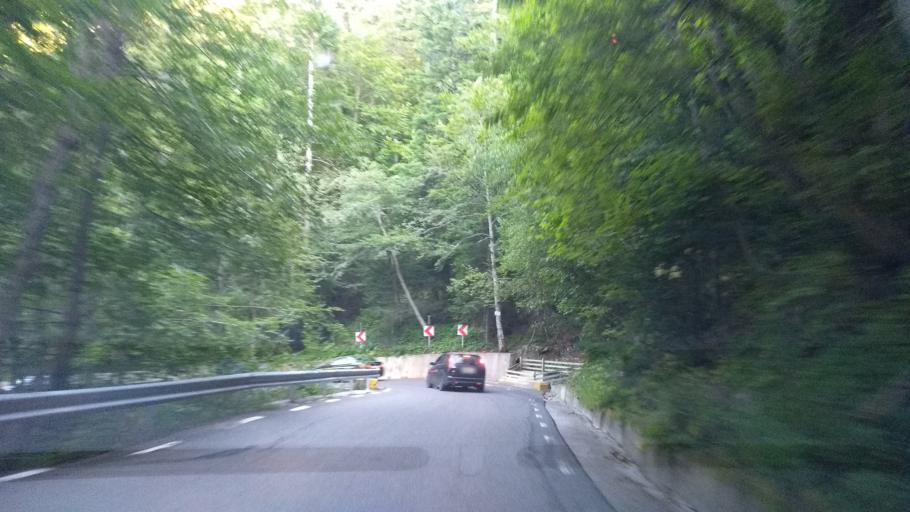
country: RO
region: Prahova
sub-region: Oras Sinaia
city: Sinaia
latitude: 45.3229
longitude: 25.4987
